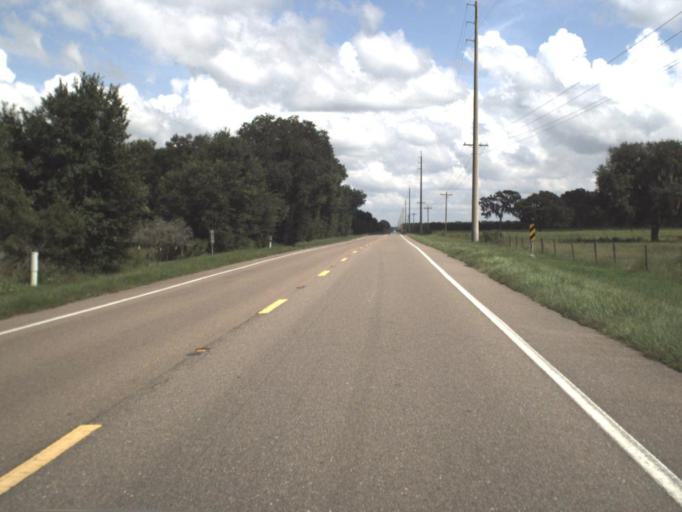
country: US
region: Florida
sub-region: Hardee County
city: Wauchula
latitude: 27.4852
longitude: -81.9987
